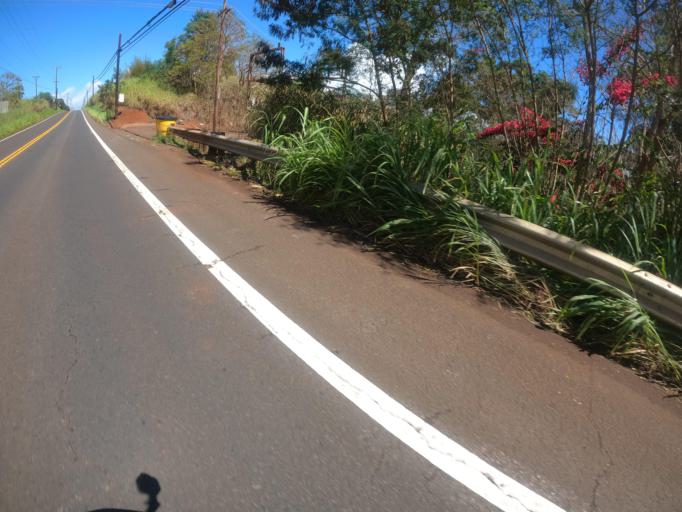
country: US
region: Hawaii
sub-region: Honolulu County
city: Schofield Barracks
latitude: 21.4588
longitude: -158.0576
